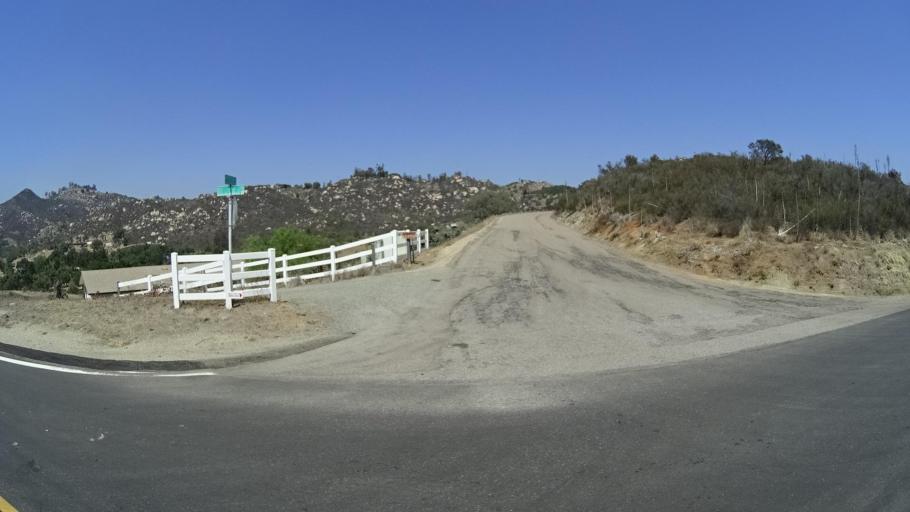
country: US
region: California
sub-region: San Diego County
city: Fallbrook
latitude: 33.4086
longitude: -117.2735
